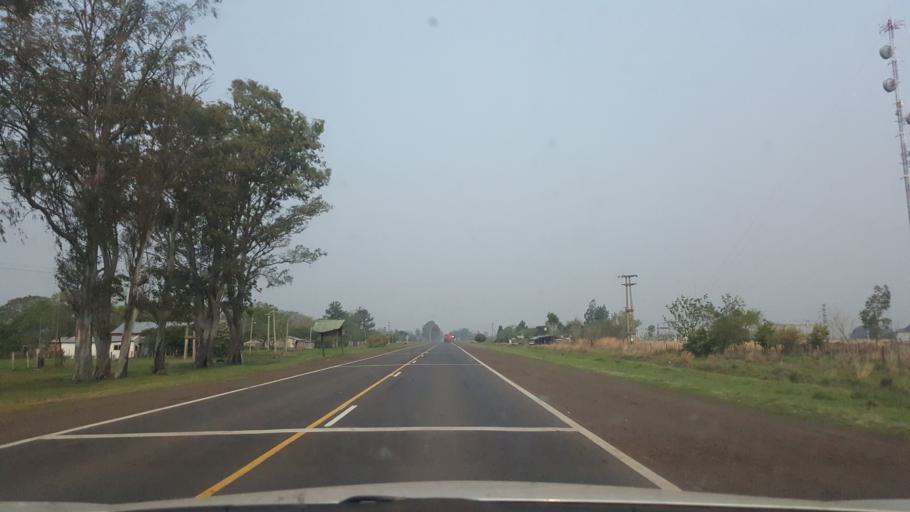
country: AR
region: Corrientes
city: Ita Ibate
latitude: -27.4433
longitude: -57.3389
